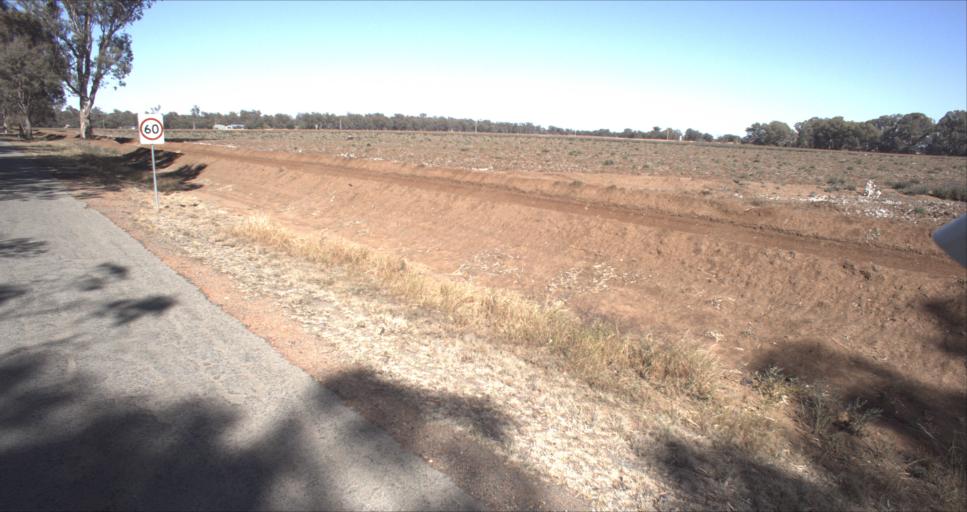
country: AU
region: New South Wales
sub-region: Leeton
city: Leeton
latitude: -34.6079
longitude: 146.2624
